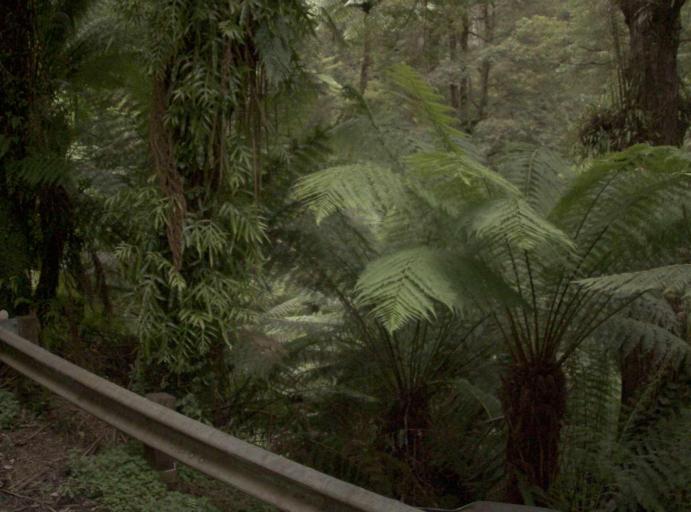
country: AU
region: Victoria
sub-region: Latrobe
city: Traralgon
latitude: -38.4482
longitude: 146.5382
